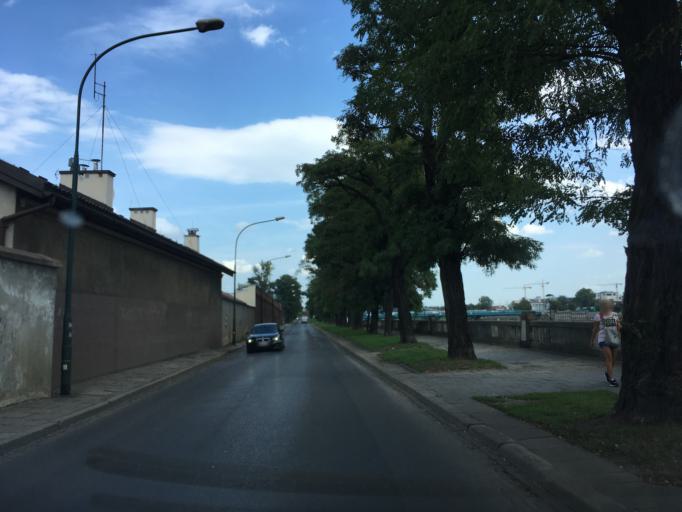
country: PL
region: Lesser Poland Voivodeship
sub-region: Krakow
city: Krakow
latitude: 50.0476
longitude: 19.9482
